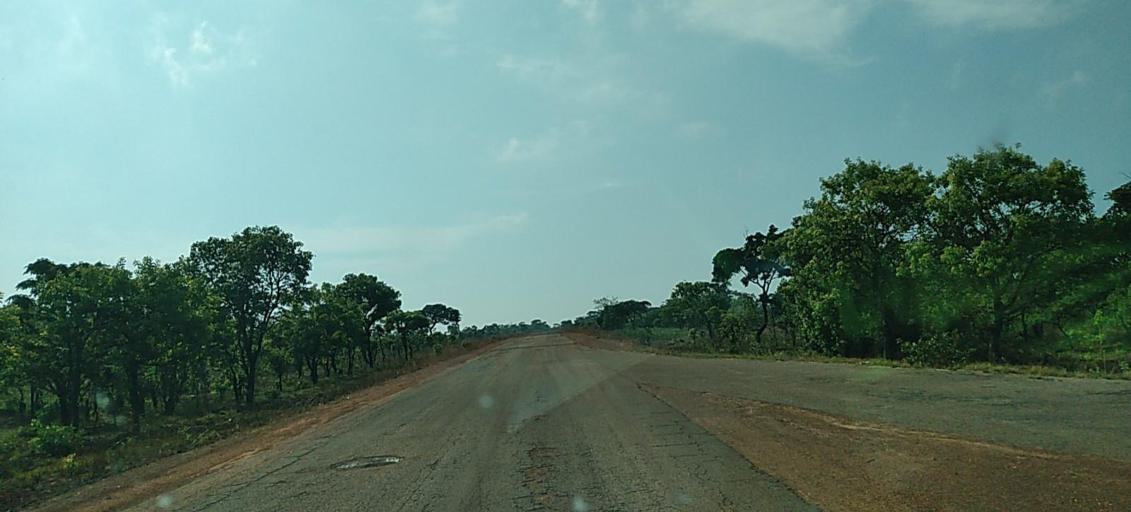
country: ZM
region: North-Western
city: Mwinilunga
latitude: -11.7735
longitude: 25.0148
